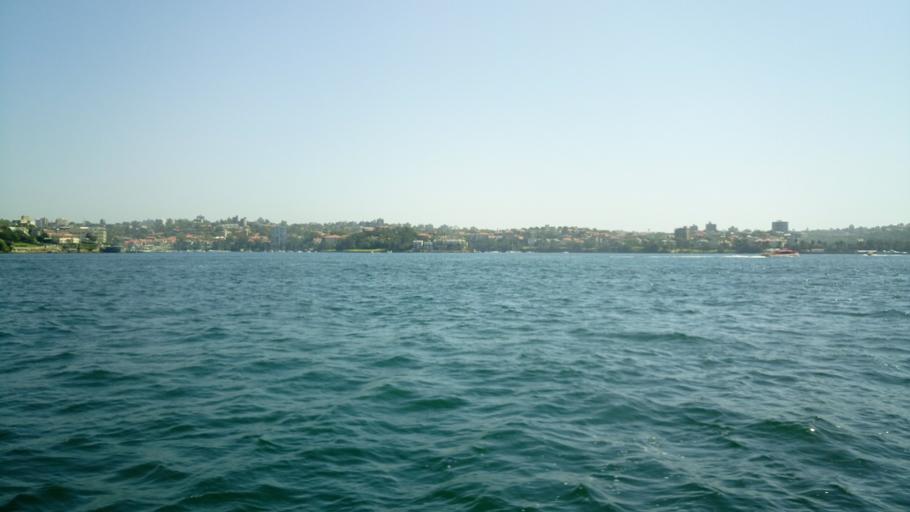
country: AU
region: New South Wales
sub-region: North Sydney
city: Kirribilli
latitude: -33.8561
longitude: 151.2220
